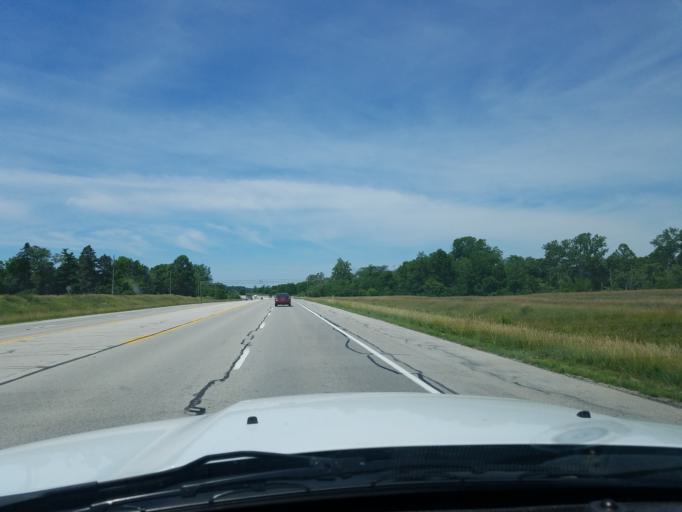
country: US
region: Indiana
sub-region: Delaware County
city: Yorktown
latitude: 40.1208
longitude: -85.4679
